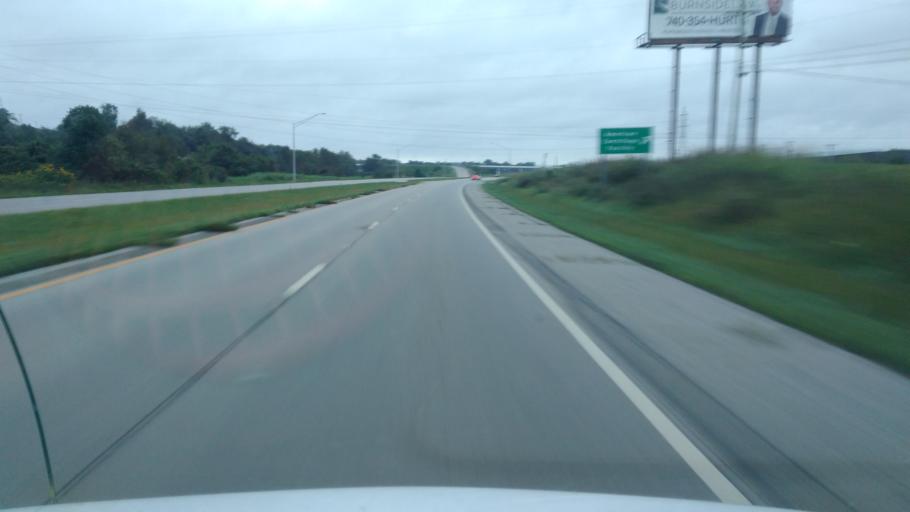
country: US
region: Ohio
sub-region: Pike County
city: Piketon
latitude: 39.0195
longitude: -83.0259
